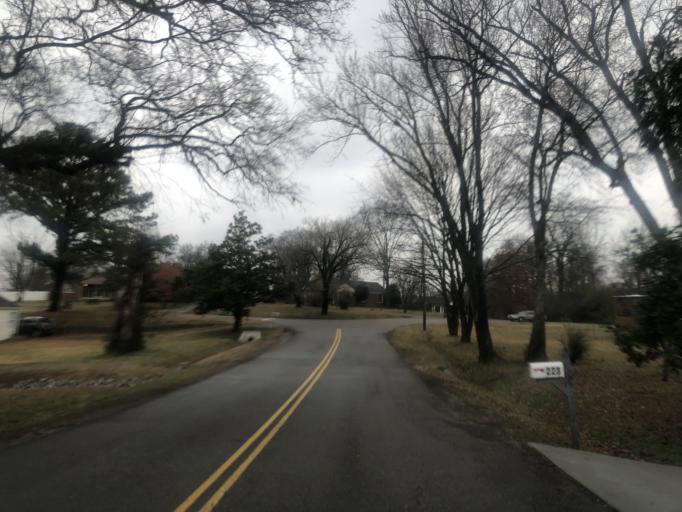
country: US
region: Tennessee
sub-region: Davidson County
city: Lakewood
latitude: 36.1731
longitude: -86.6922
